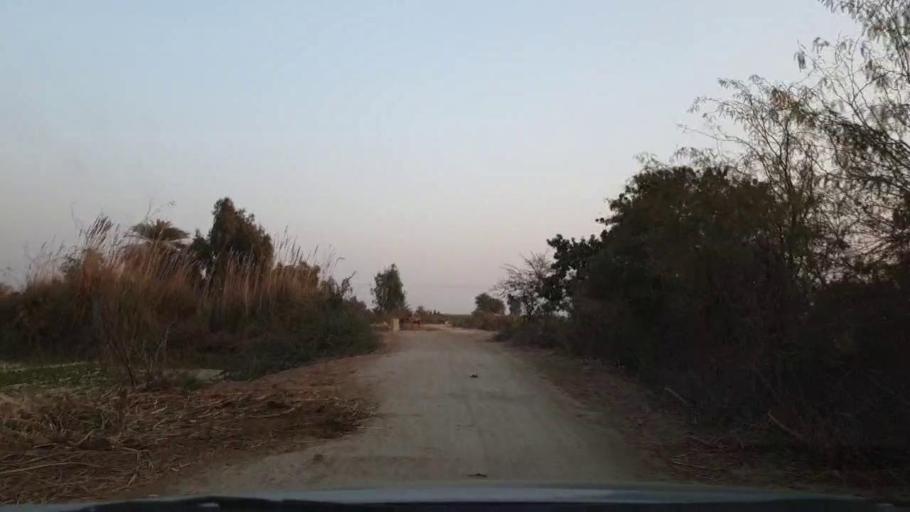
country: PK
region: Sindh
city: Matiari
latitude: 25.6862
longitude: 68.5232
